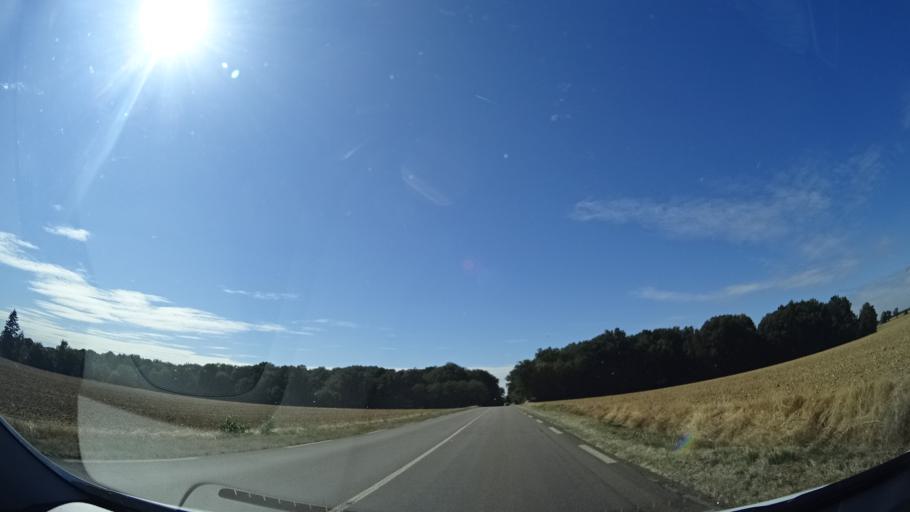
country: FR
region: Bourgogne
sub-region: Departement de l'Yonne
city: Charny
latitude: 47.9328
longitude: 3.1672
